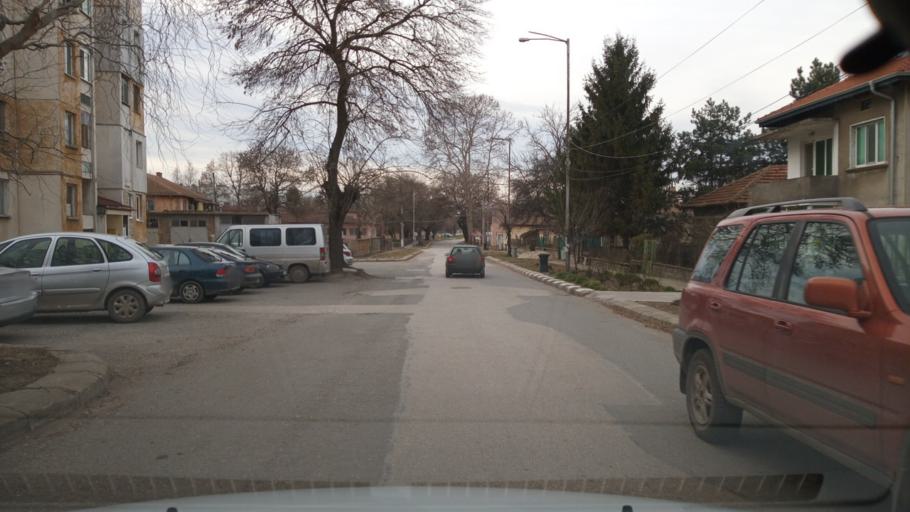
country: BG
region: Pleven
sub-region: Obshtina Belene
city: Belene
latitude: 43.6457
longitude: 25.1224
